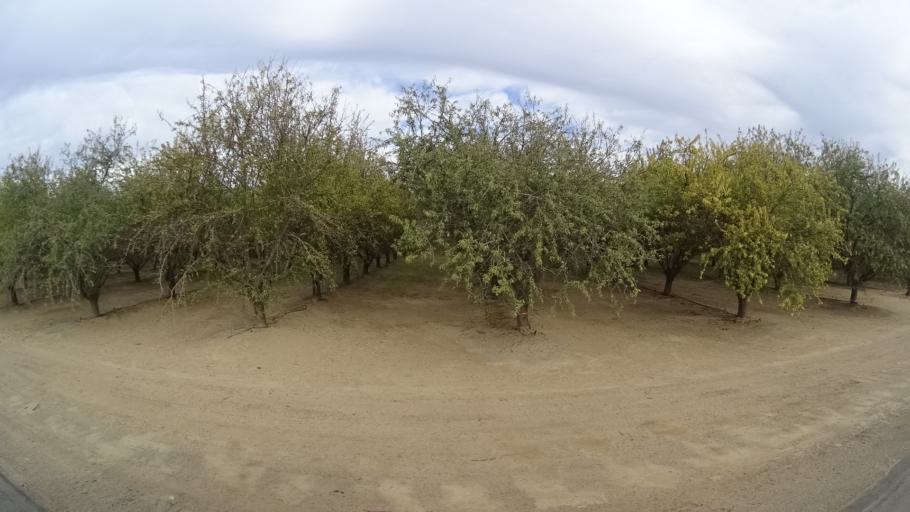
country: US
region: California
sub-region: Kern County
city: Rosedale
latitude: 35.4198
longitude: -119.1745
